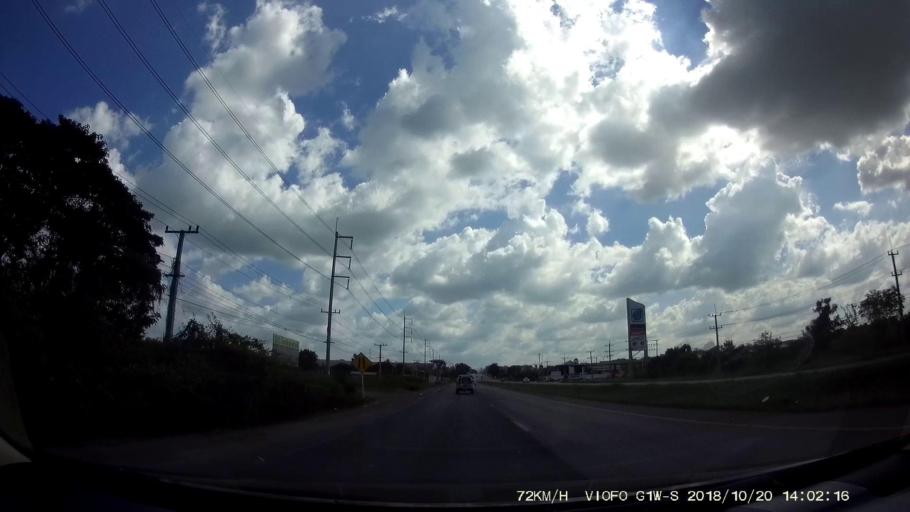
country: TH
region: Khon Kaen
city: Chum Phae
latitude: 16.4936
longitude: 102.1248
